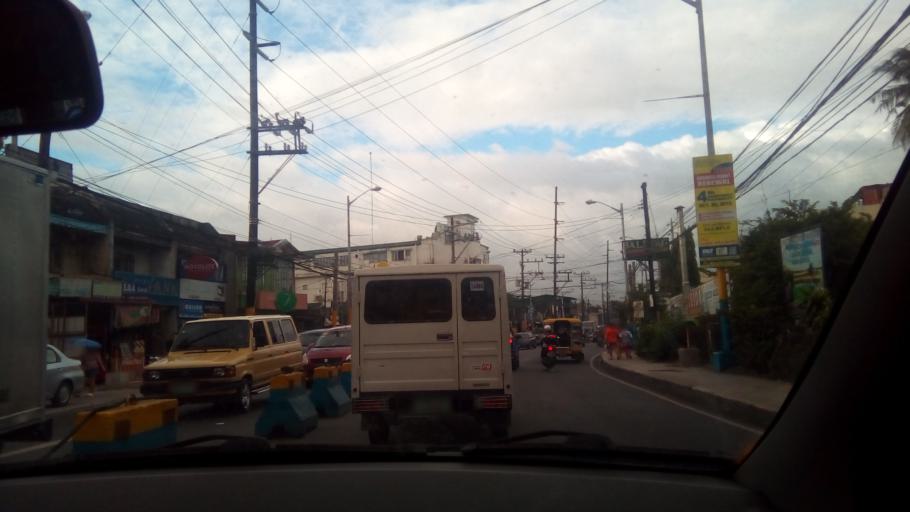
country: PH
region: Calabarzon
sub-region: Province of Laguna
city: San Pedro
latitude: 14.3901
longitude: 121.0446
